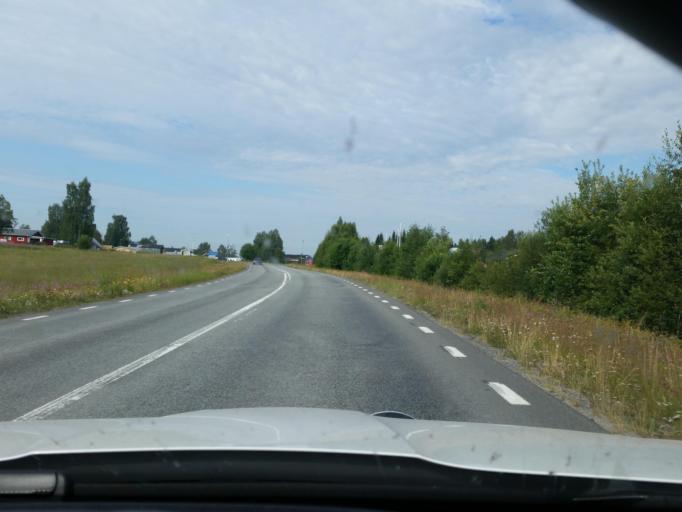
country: SE
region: Norrbotten
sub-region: Alvsbyns Kommun
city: AElvsbyn
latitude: 65.6687
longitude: 20.8749
